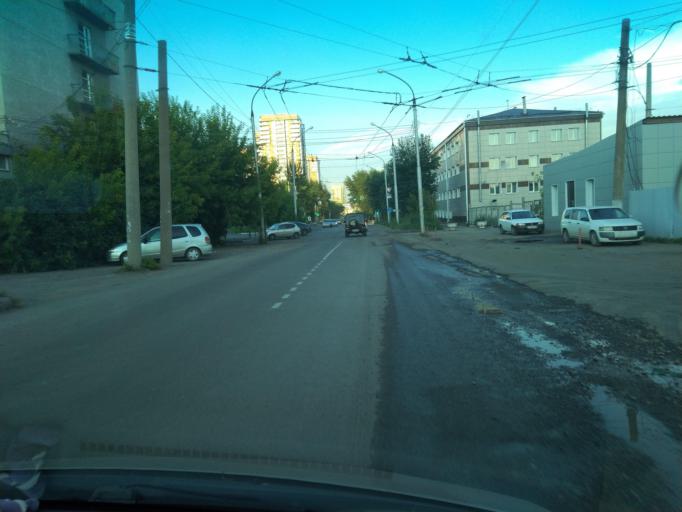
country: RU
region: Krasnoyarskiy
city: Krasnoyarsk
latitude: 56.0313
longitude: 92.9050
